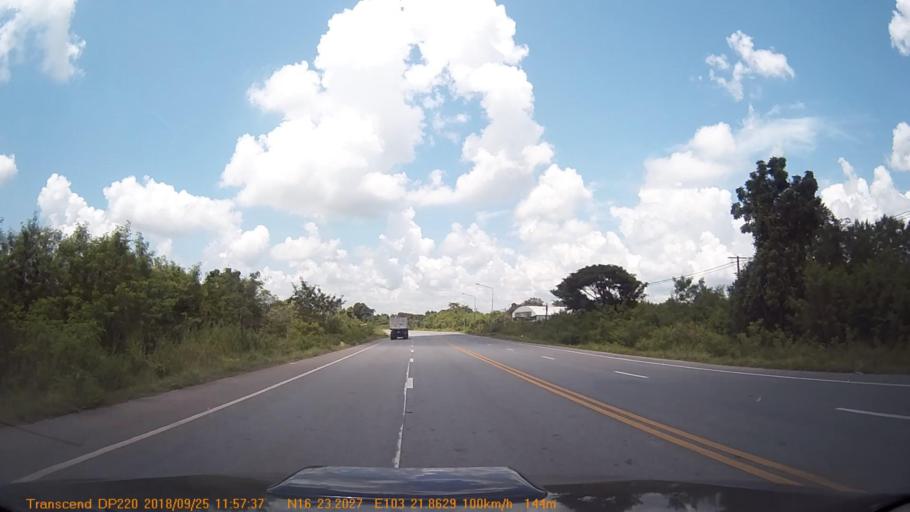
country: TH
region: Kalasin
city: Yang Talat
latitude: 16.3867
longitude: 103.3644
